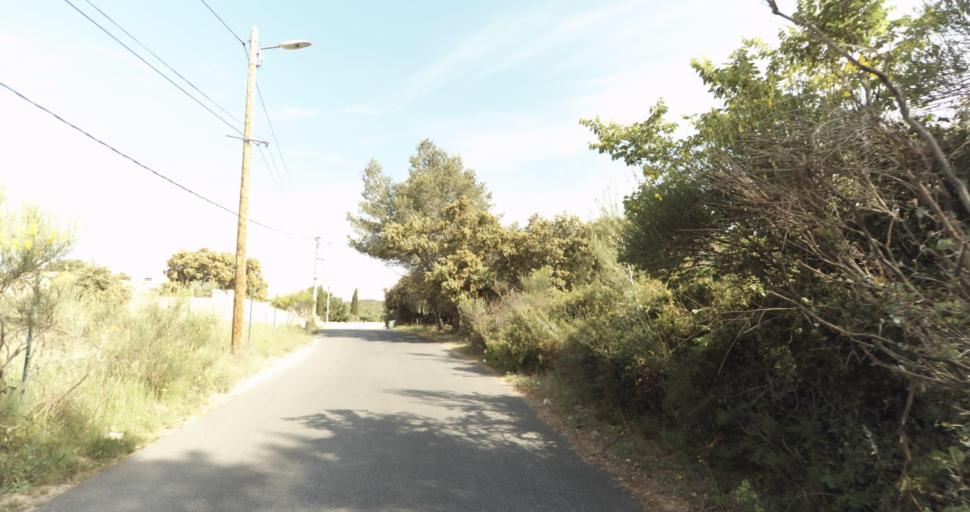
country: FR
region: Languedoc-Roussillon
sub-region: Departement du Gard
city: Poulx
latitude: 43.8738
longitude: 4.3933
